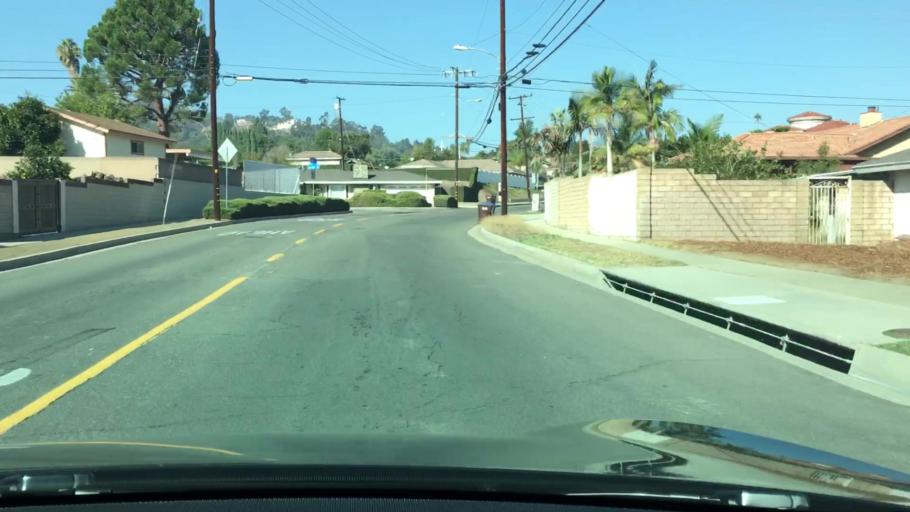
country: US
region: California
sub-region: Los Angeles County
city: Hacienda Heights
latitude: 33.9957
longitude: -117.9776
